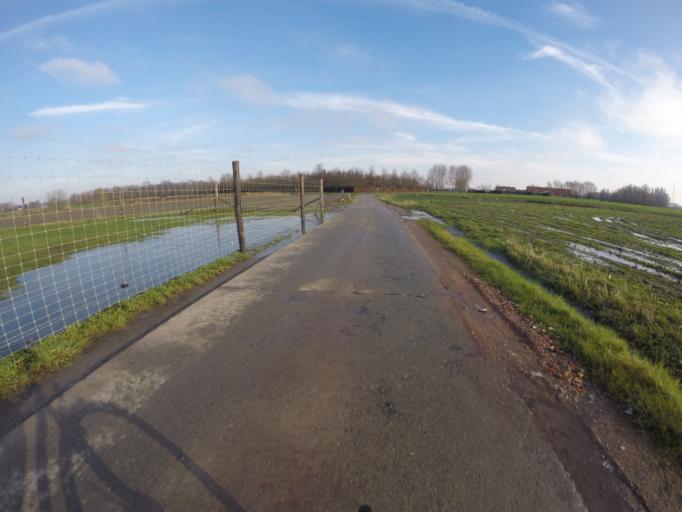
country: BE
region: Flanders
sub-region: Provincie Oost-Vlaanderen
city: Nevele
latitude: 51.0414
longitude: 3.5173
